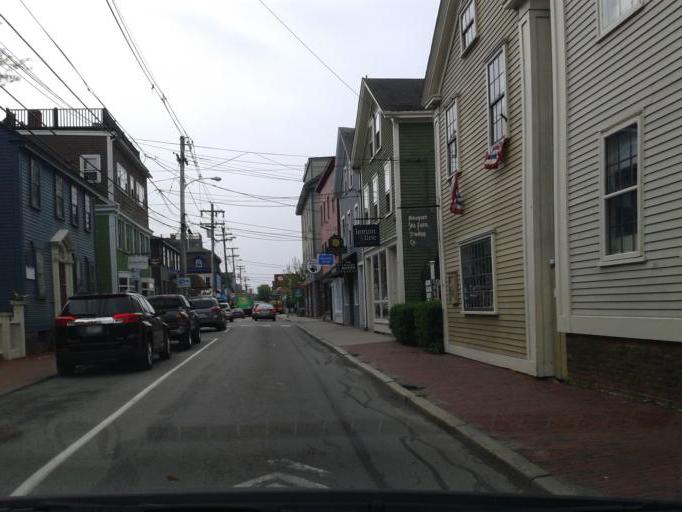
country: US
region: Rhode Island
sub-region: Newport County
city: Newport
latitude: 41.4822
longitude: -71.3145
